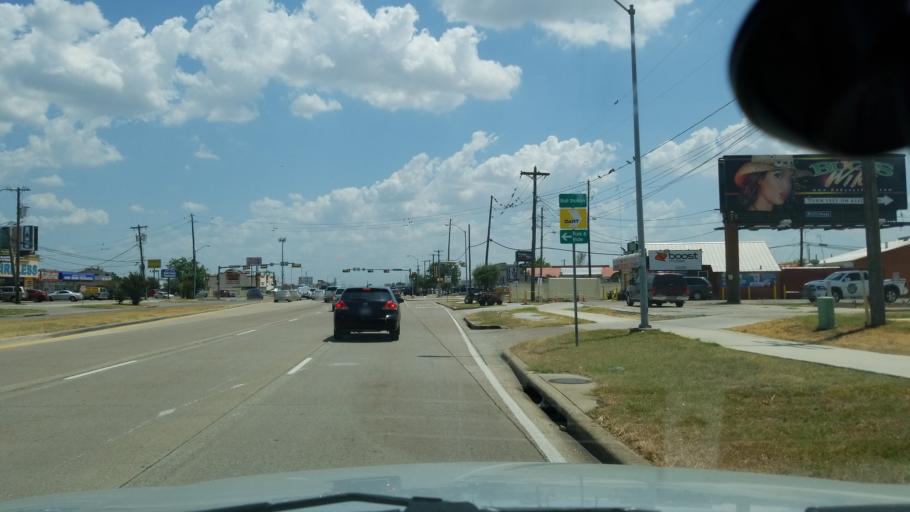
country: US
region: Texas
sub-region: Dallas County
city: Farmers Branch
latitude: 32.8969
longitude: -96.8919
